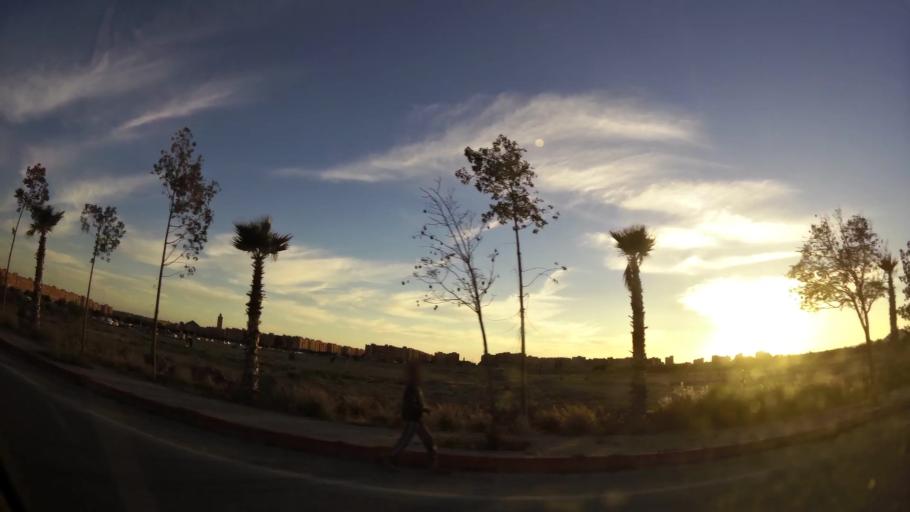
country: MA
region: Marrakech-Tensift-Al Haouz
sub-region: Marrakech
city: Marrakesh
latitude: 31.7552
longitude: -8.1116
